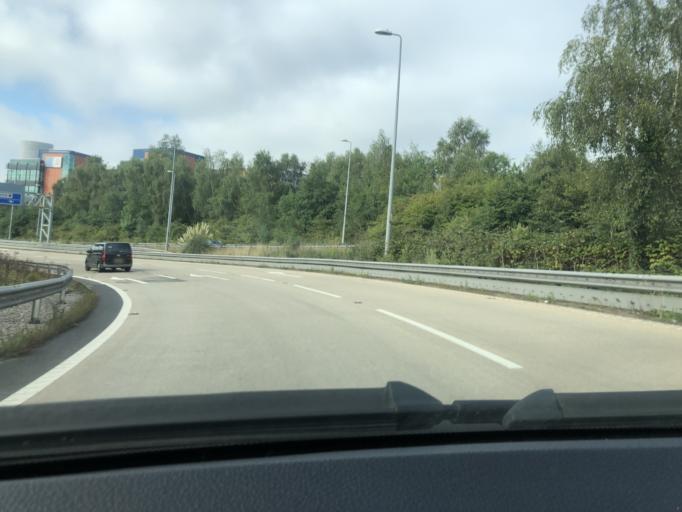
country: GB
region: England
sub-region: Devon
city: Heavitree
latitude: 50.7302
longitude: -3.4647
